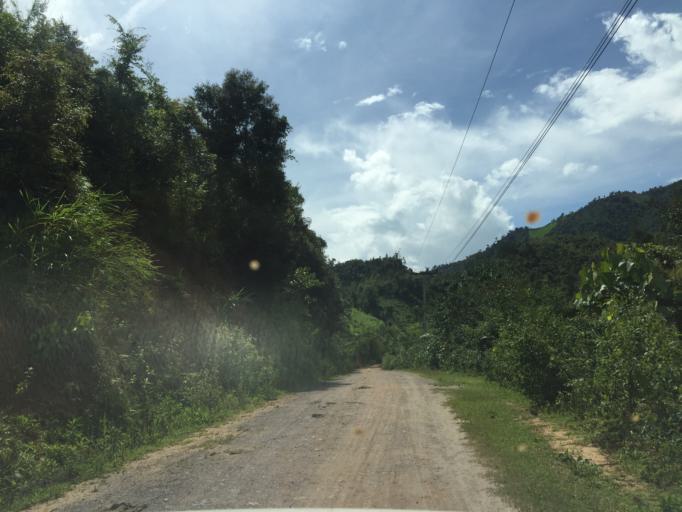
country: LA
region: Xiangkhoang
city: Muang Phonsavan
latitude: 19.3375
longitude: 103.5202
